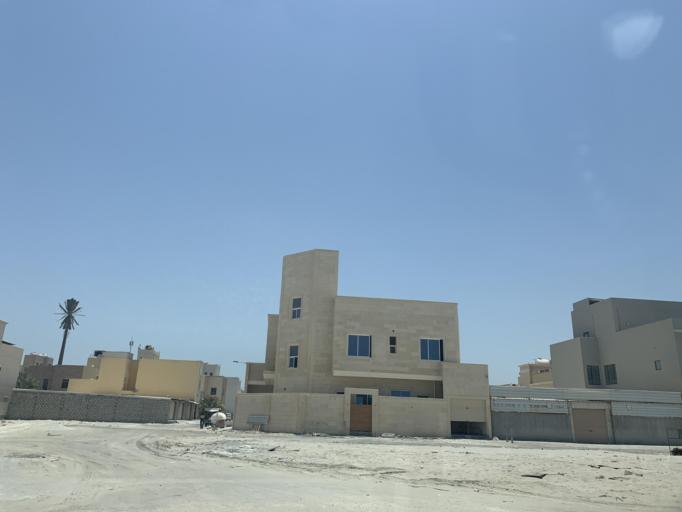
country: BH
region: Muharraq
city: Al Muharraq
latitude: 26.2866
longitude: 50.6182
